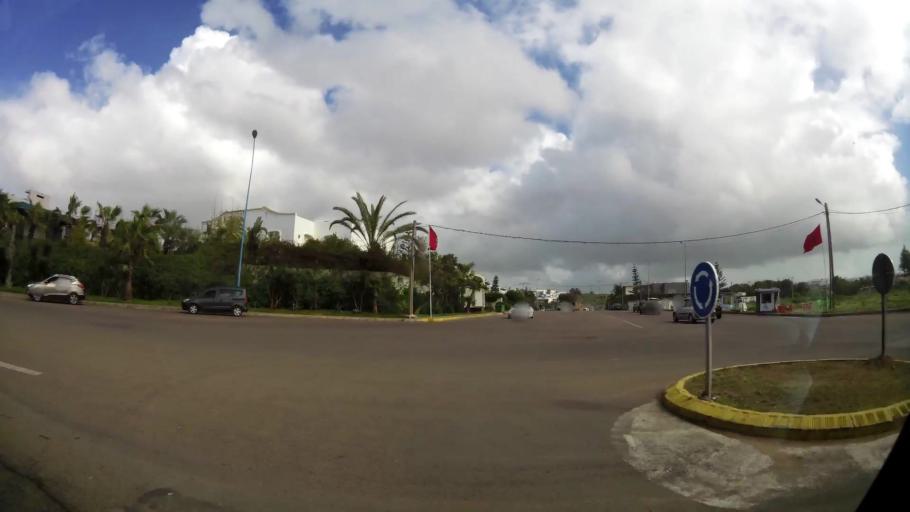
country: MA
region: Grand Casablanca
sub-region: Casablanca
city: Casablanca
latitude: 33.5707
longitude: -7.7086
